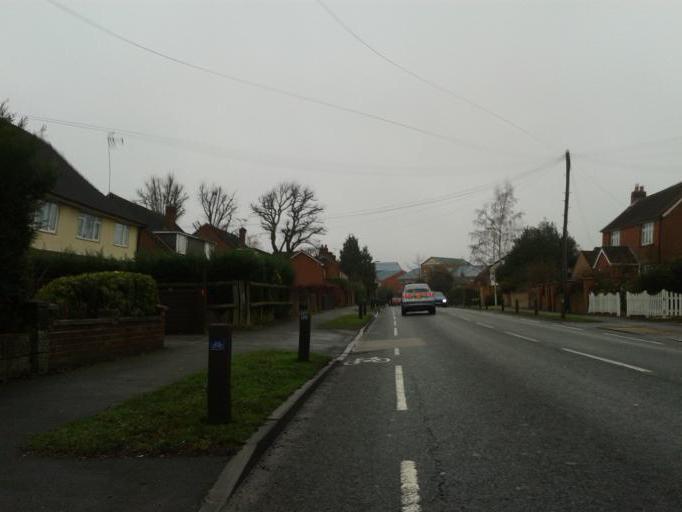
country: GB
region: England
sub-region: Hampshire
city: Farnborough
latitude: 51.2939
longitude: -0.7801
